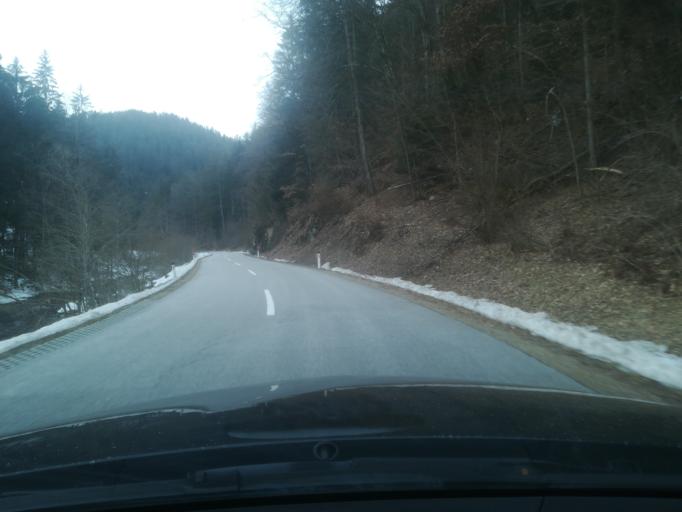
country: AT
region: Upper Austria
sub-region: Politischer Bezirk Perg
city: Perg
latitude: 48.4004
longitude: 14.6374
